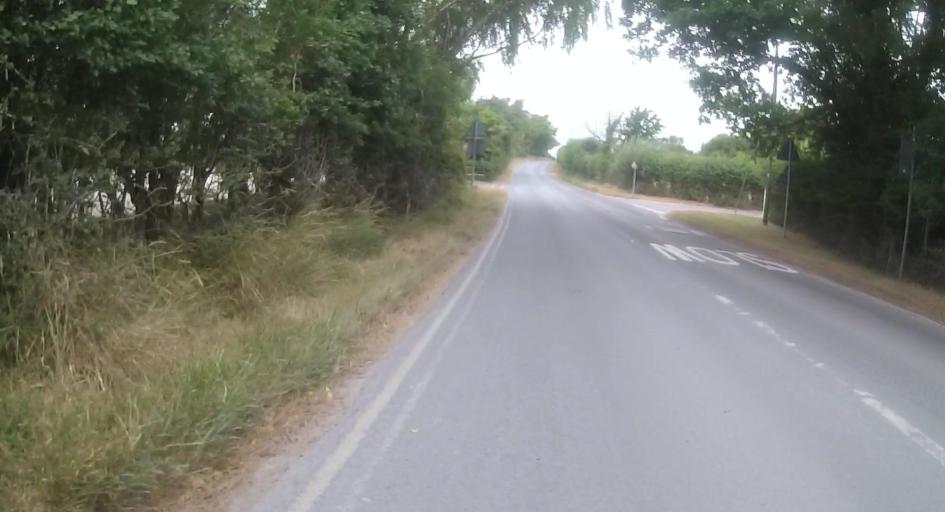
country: GB
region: England
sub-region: Dorset
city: Wareham
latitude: 50.6582
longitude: -2.1001
